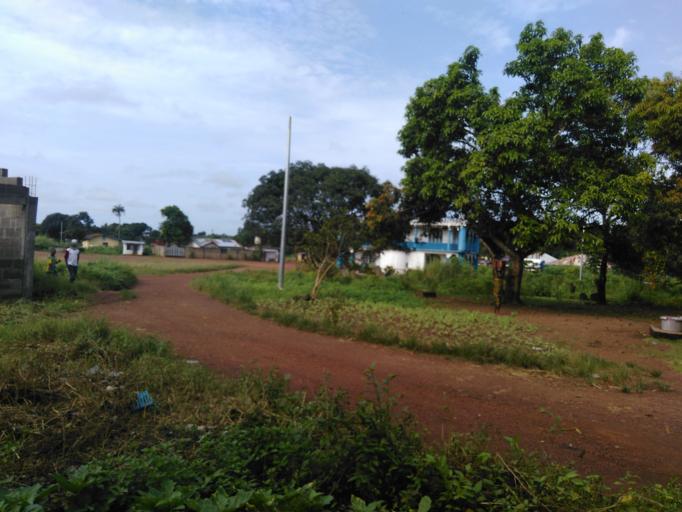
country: SL
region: Southern Province
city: Rotifunk
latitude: 8.4867
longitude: -12.7561
